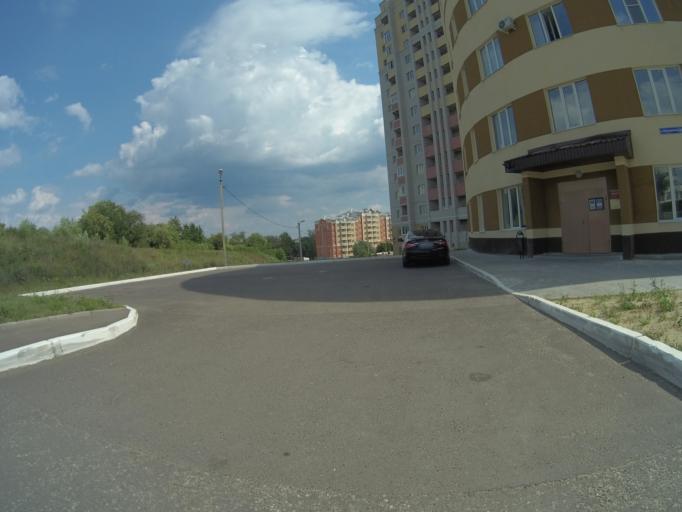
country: RU
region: Vladimir
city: Vladimir
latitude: 56.1333
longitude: 40.3801
